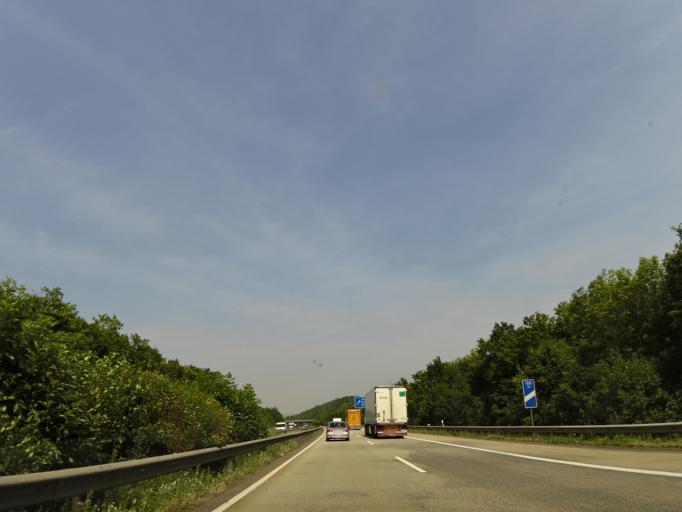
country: DE
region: Rheinland-Pfalz
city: Konigsfeld
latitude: 50.5240
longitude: 7.1915
